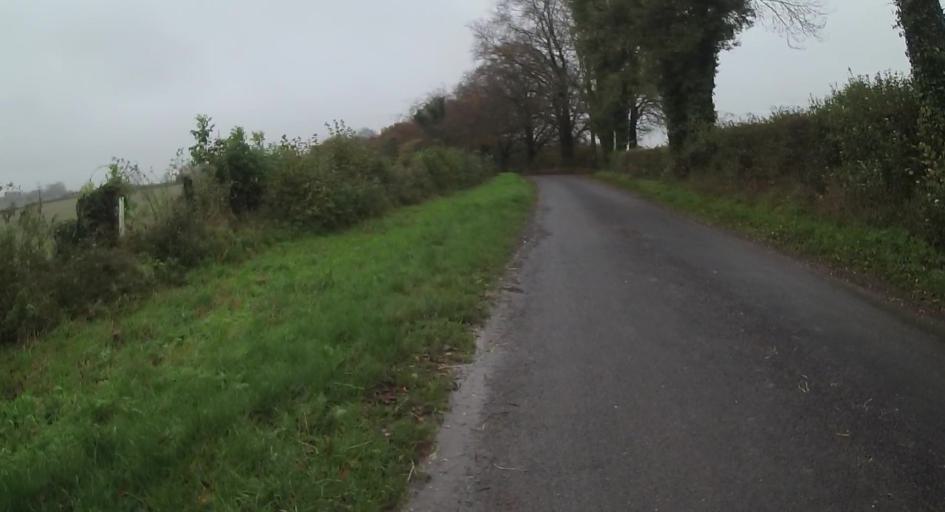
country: GB
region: England
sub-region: Hampshire
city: Four Marks
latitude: 51.1519
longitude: -1.1175
